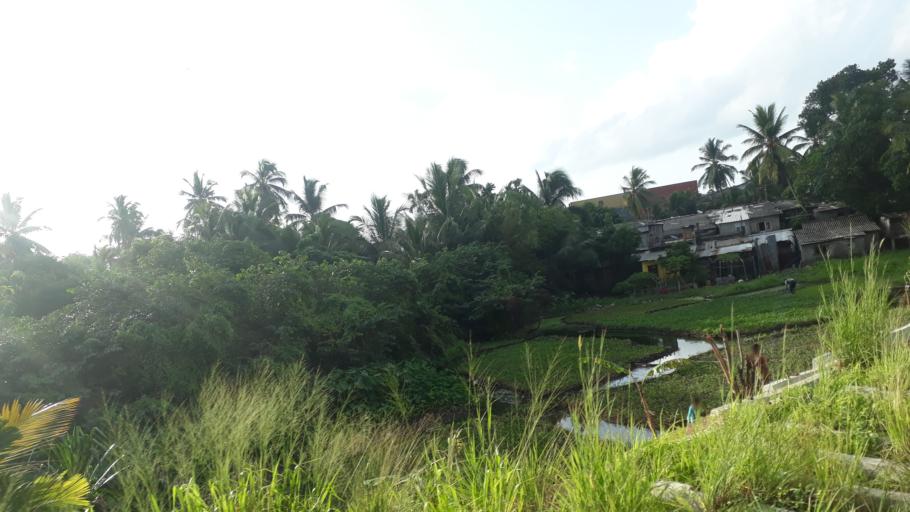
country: LK
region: Western
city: Kolonnawa
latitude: 6.9488
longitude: 79.8876
